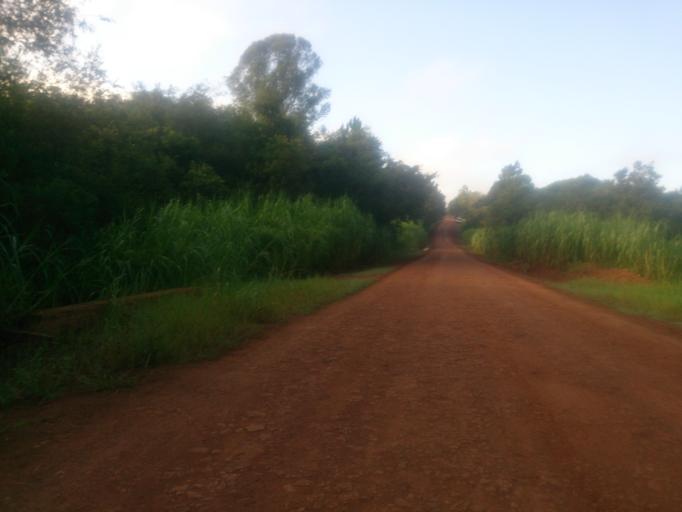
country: AR
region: Misiones
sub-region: Departamento de Obera
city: Obera
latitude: -27.4640
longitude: -55.1061
